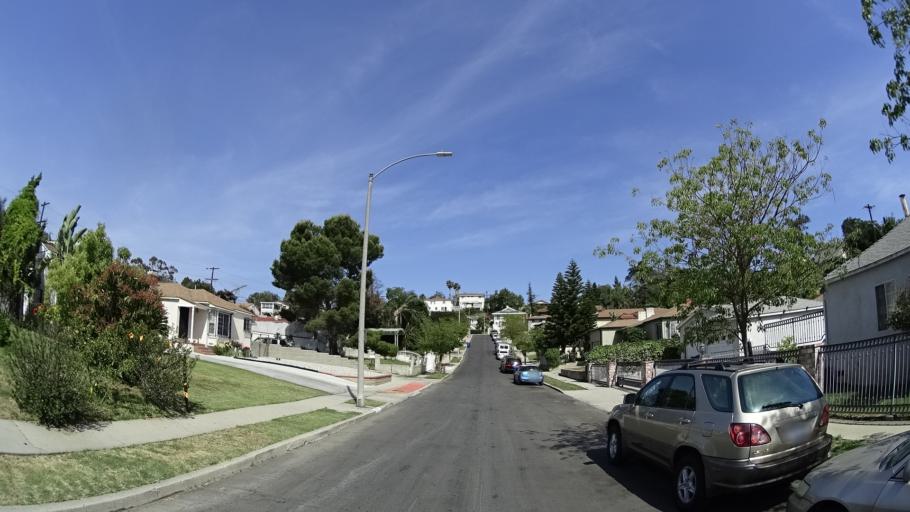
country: US
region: California
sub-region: Los Angeles County
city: Belvedere
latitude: 34.0656
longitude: -118.1860
